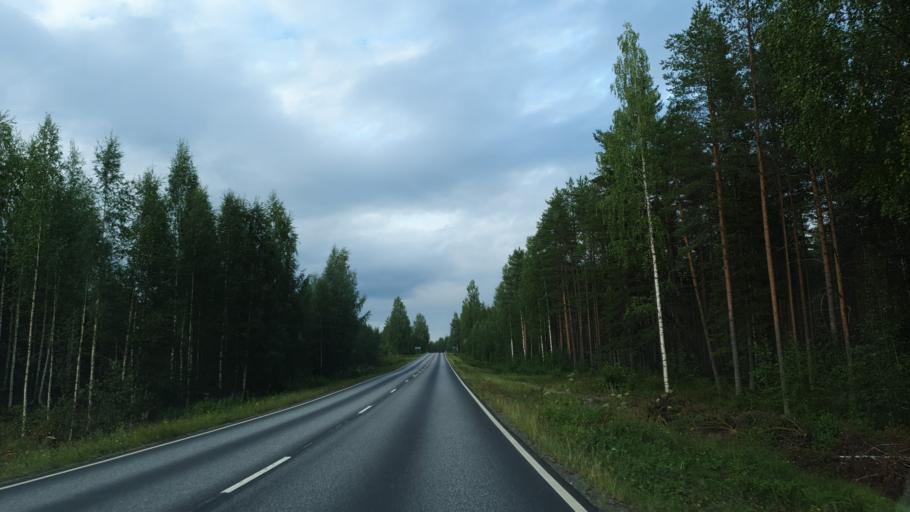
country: FI
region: North Karelia
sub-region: Joensuu
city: Eno
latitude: 63.0357
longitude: 30.1092
